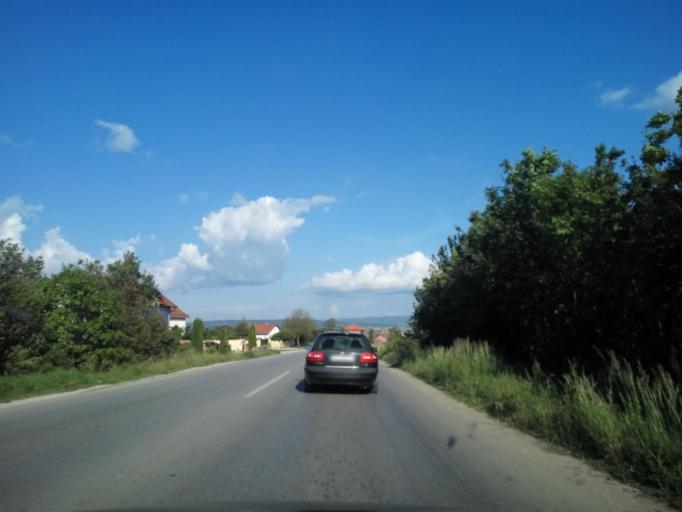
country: XK
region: Prizren
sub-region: Komuna e Malisheves
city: Llazice
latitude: 42.5866
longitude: 20.6844
